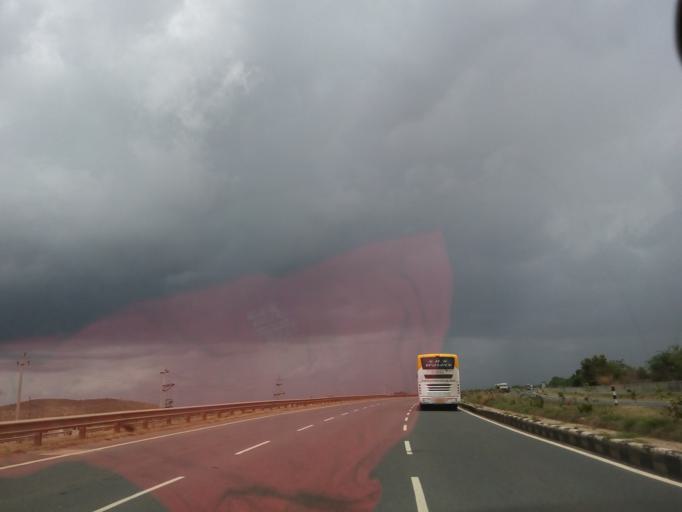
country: IN
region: Karnataka
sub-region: Chitradurga
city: Chitradurga
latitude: 14.1584
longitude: 76.4821
